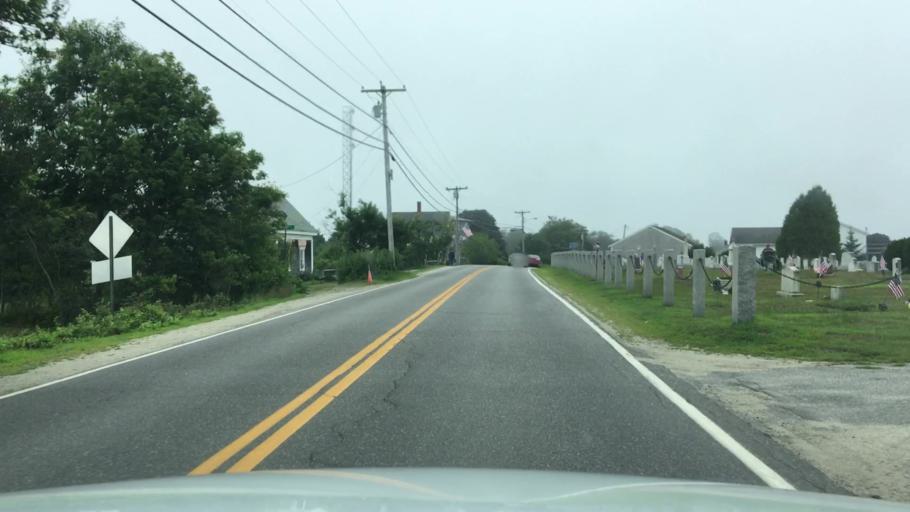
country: US
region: Maine
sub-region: Cumberland County
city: Harpswell Center
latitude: 43.7391
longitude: -69.9941
